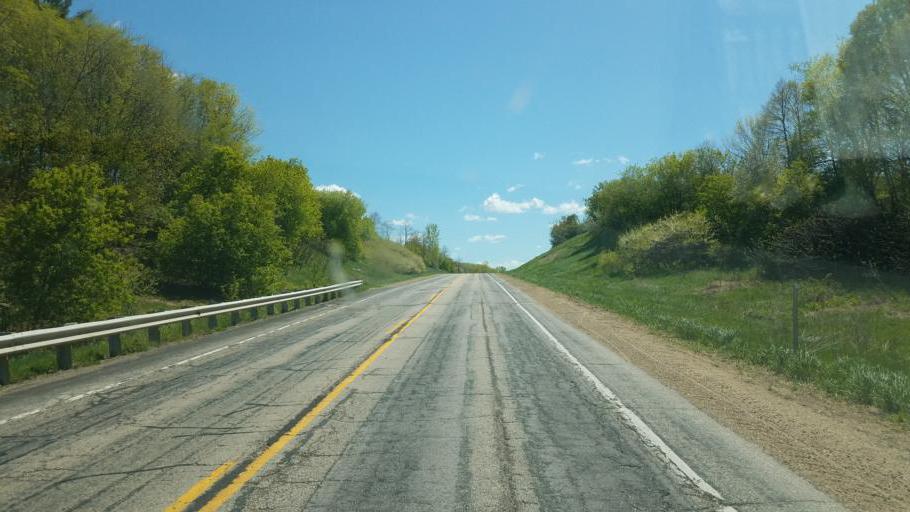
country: US
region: Wisconsin
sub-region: Vernon County
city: Hillsboro
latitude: 43.5974
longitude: -90.3523
